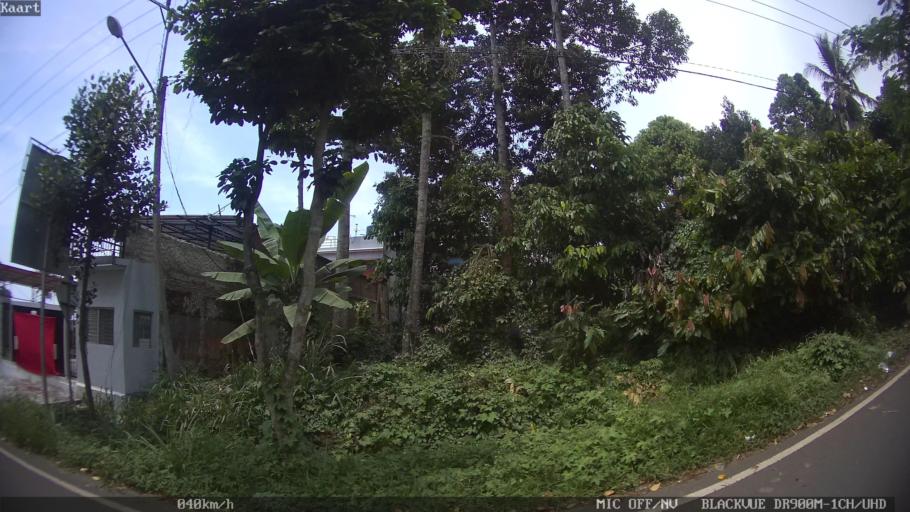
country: ID
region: Lampung
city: Bandarlampung
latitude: -5.4333
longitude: 105.2441
